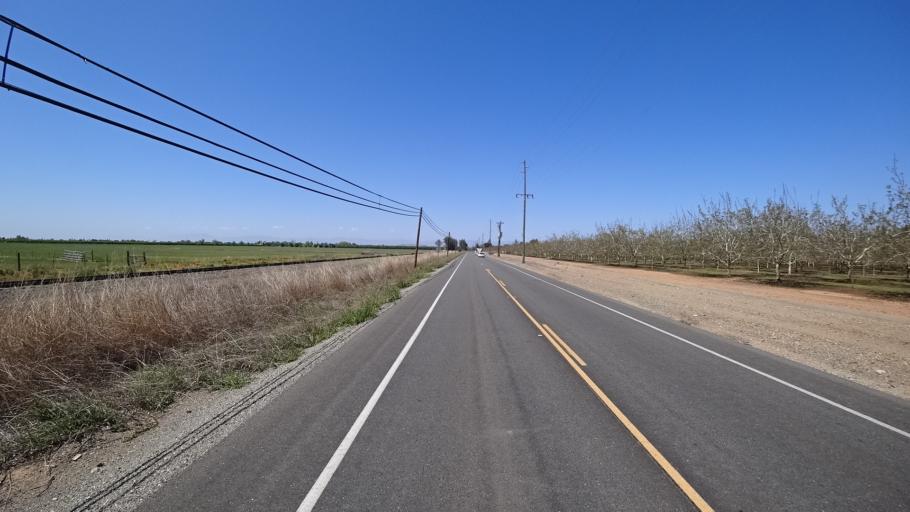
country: US
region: California
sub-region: Glenn County
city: Orland
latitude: 39.7688
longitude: -122.1704
